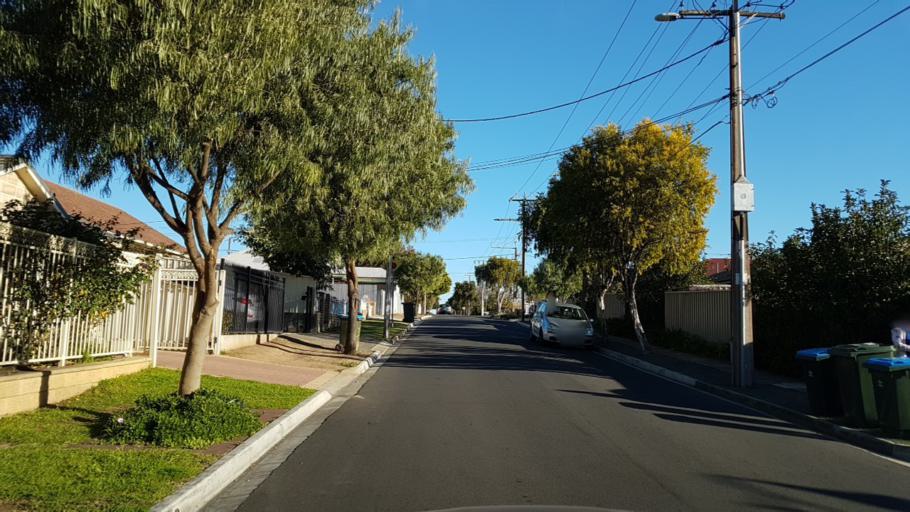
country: AU
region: South Australia
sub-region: Campbelltown
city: Campbelltown
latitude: -34.8772
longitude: 138.6575
